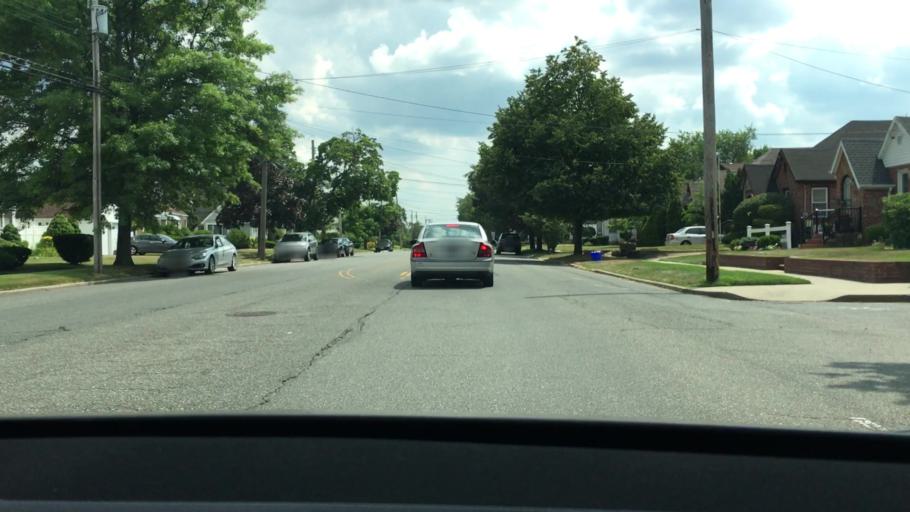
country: US
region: New York
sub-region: Nassau County
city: North Valley Stream
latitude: 40.6766
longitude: -73.6924
